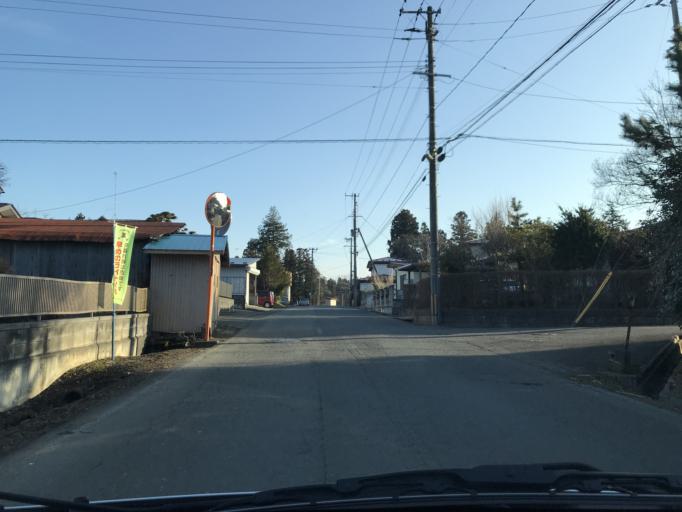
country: JP
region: Iwate
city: Mizusawa
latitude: 39.2058
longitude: 141.1180
